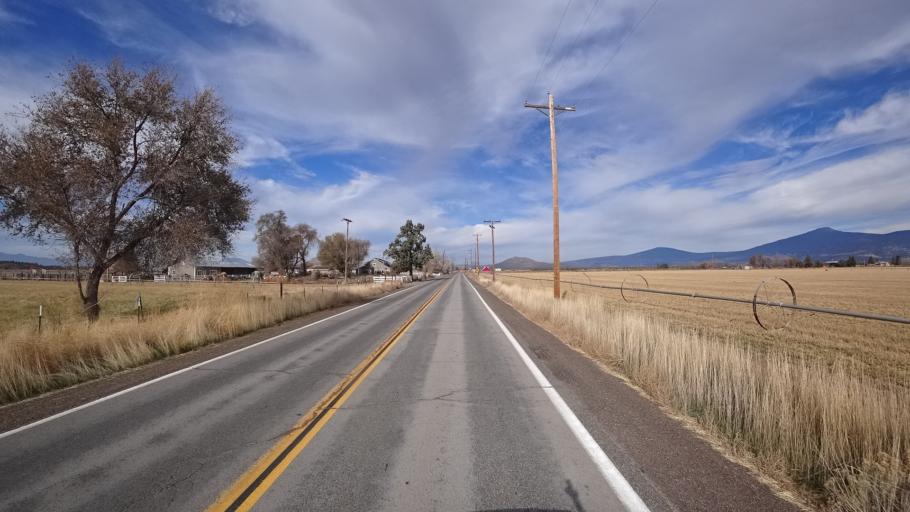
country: US
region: California
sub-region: Siskiyou County
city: Montague
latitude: 41.6136
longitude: -122.3996
